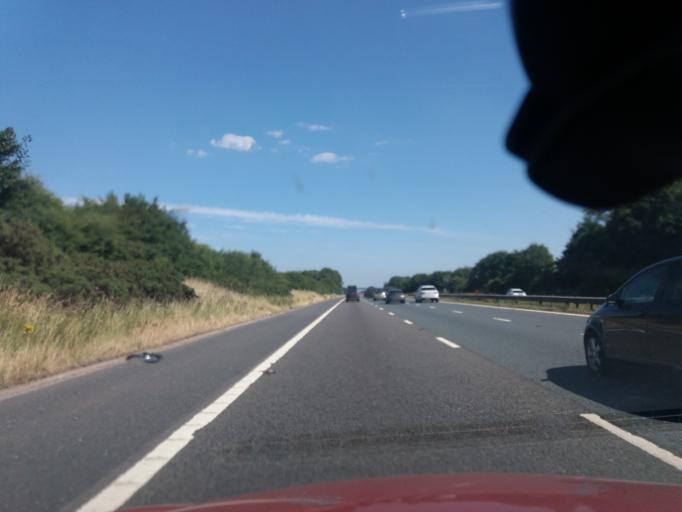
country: GB
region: England
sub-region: Borough of Wigan
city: Tyldesley
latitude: 53.5478
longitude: -2.4636
